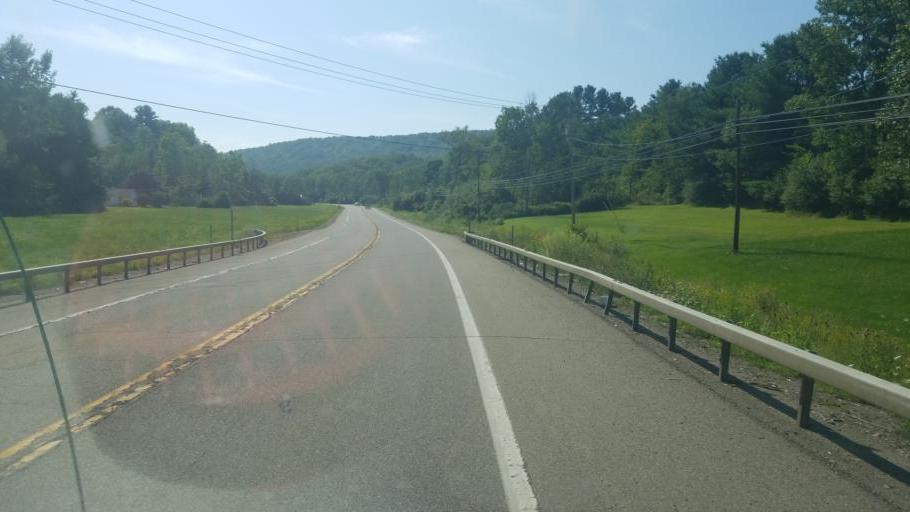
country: US
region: New York
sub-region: Allegany County
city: Wellsville
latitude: 42.1247
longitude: -77.9902
